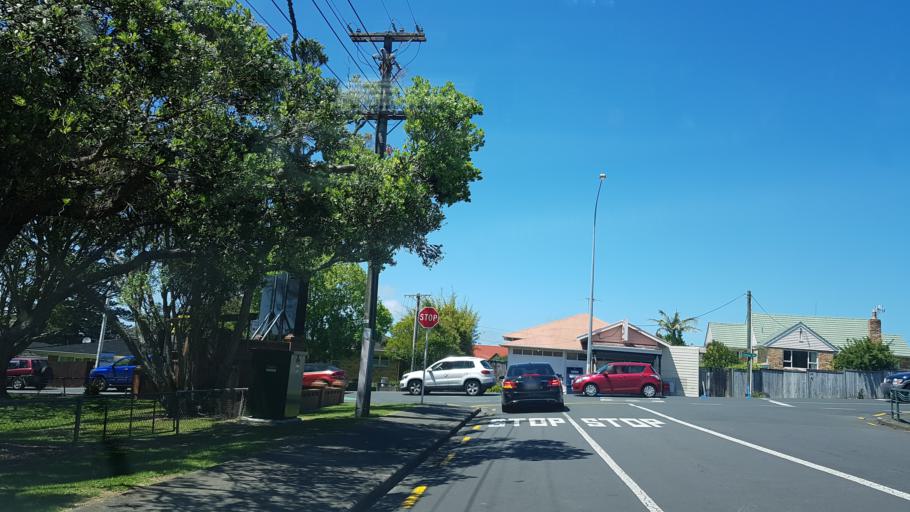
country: NZ
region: Auckland
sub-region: Auckland
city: North Shore
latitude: -36.8099
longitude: 174.7335
